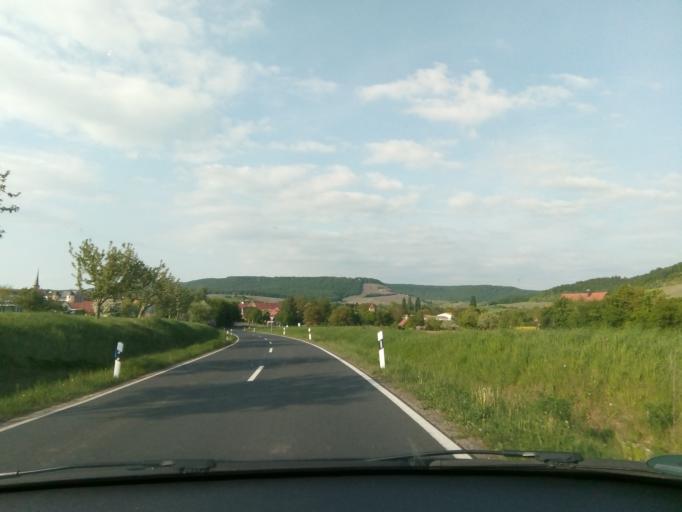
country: DE
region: Bavaria
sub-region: Regierungsbezirk Unterfranken
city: Oberschwarzach
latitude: 49.8557
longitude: 10.4095
